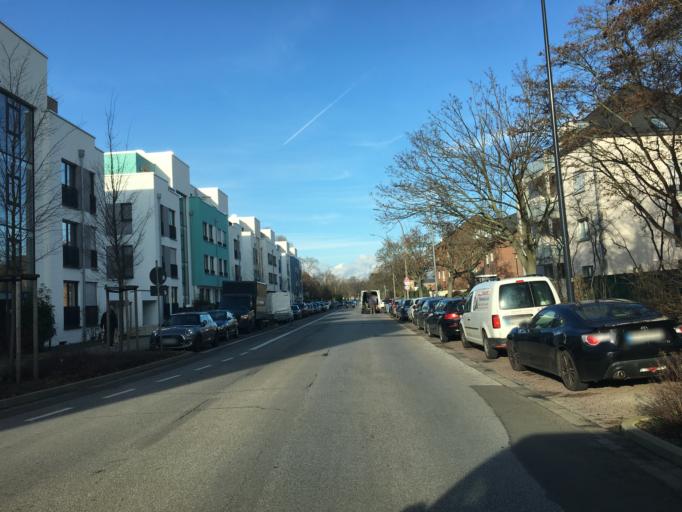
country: DE
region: North Rhine-Westphalia
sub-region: Regierungsbezirk Koln
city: Hurth
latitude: 50.8781
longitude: 6.8852
